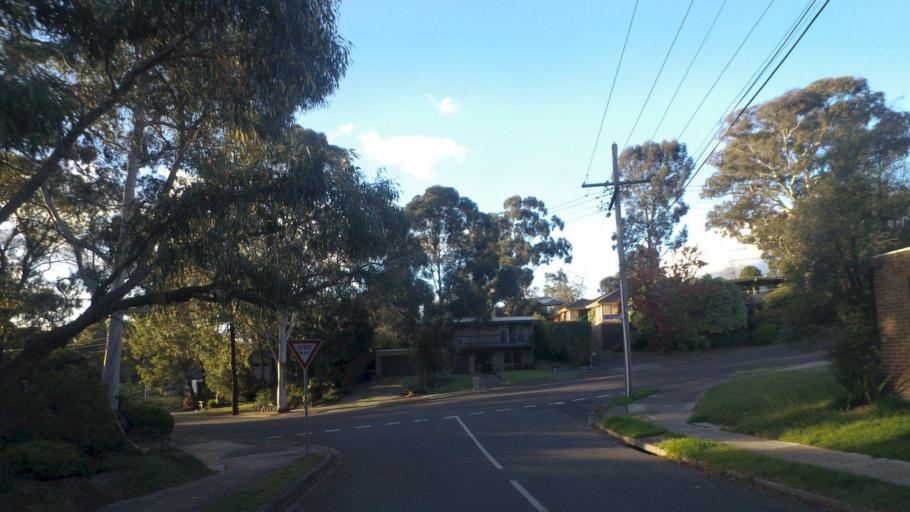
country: AU
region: Victoria
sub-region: Banyule
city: Lower Plenty
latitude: -37.7275
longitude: 145.1187
